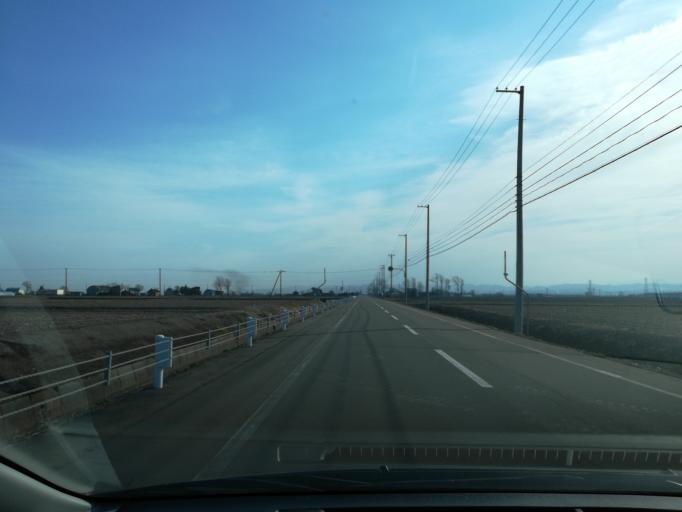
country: JP
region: Hokkaido
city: Iwamizawa
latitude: 43.1751
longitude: 141.6773
